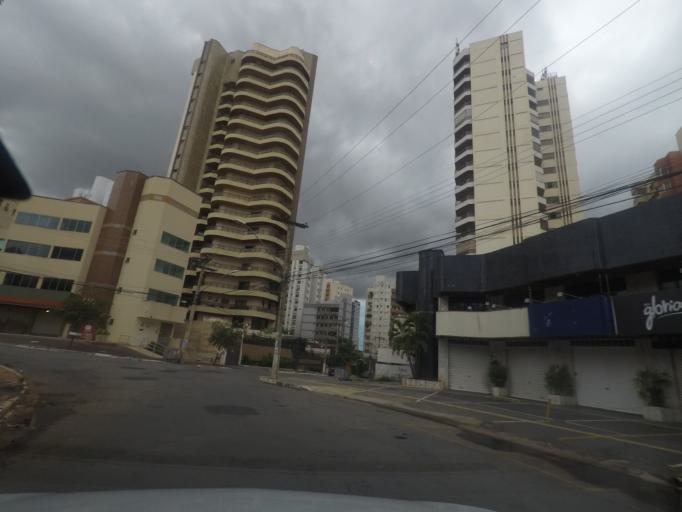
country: BR
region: Goias
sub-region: Goiania
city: Goiania
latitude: -16.6822
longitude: -49.2675
